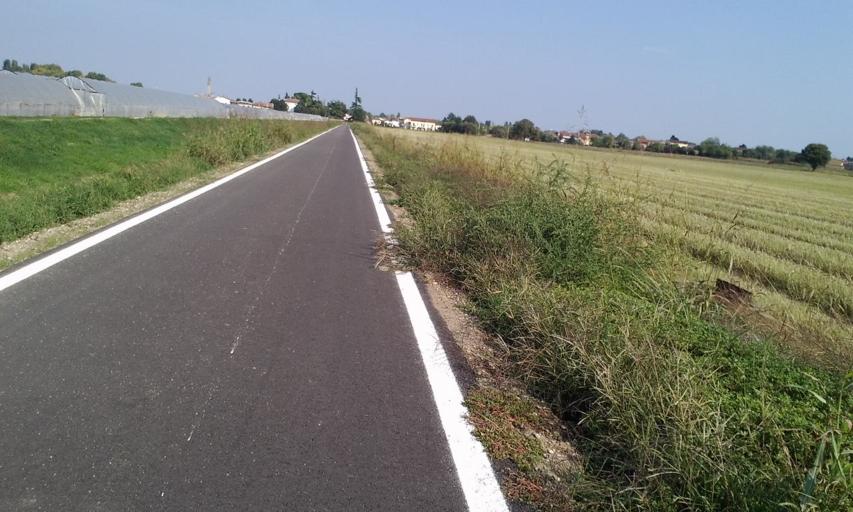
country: IT
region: Veneto
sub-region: Provincia di Verona
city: Forette
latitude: 45.3451
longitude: 10.9351
